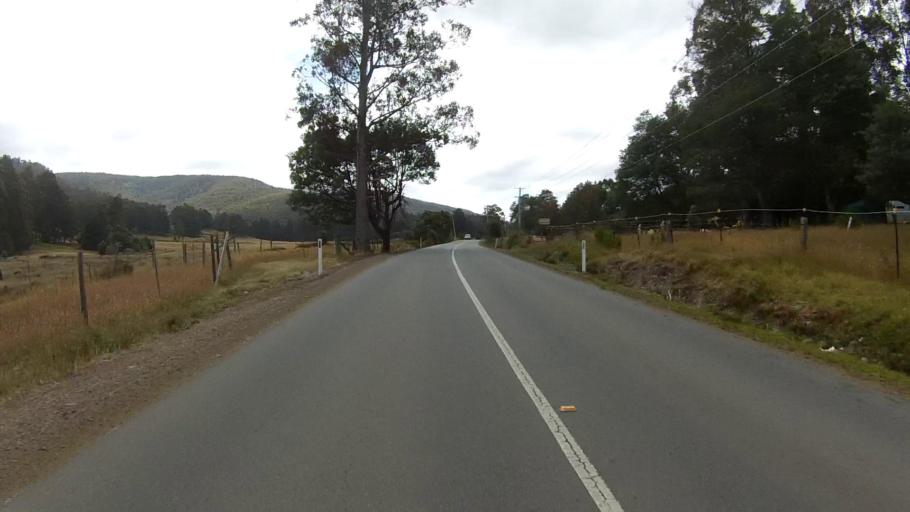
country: AU
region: Tasmania
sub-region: Kingborough
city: Kettering
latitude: -43.1212
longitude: 147.1847
